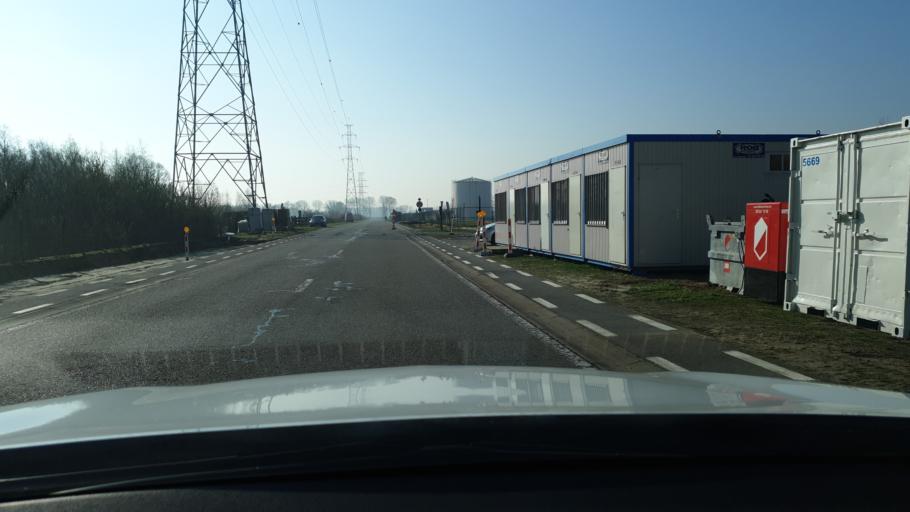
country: BE
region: Flanders
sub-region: Provincie Antwerpen
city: Zwijndrecht
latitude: 51.2448
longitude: 4.2883
